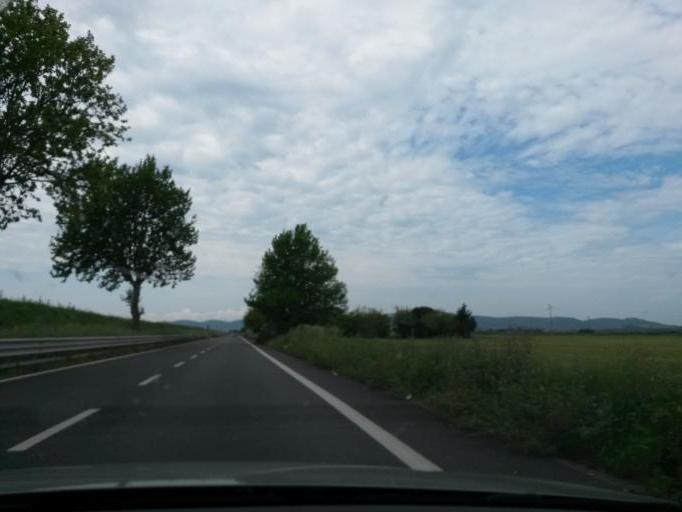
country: IT
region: Tuscany
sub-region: Provincia di Livorno
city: Venturina
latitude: 43.0002
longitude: 10.5832
